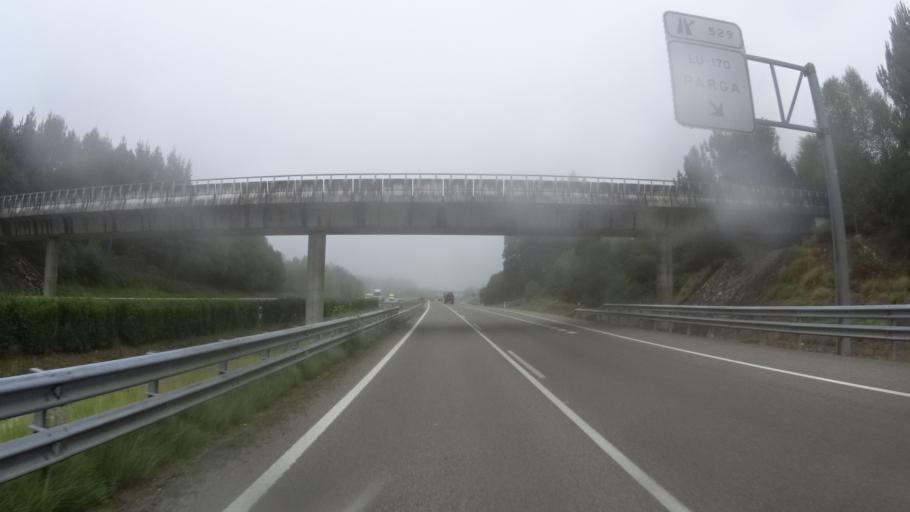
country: ES
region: Galicia
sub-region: Provincia de Lugo
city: Guitiriz
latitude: 43.1827
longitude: -7.8179
